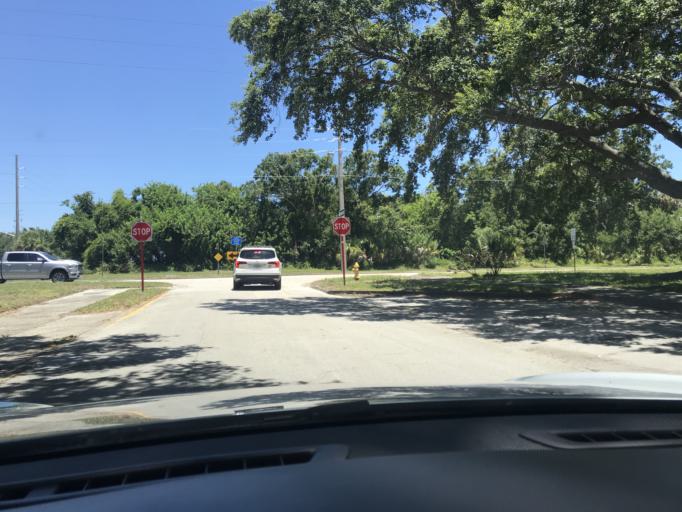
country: US
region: Florida
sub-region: Indian River County
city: Vero Beach
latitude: 27.6453
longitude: -80.4052
